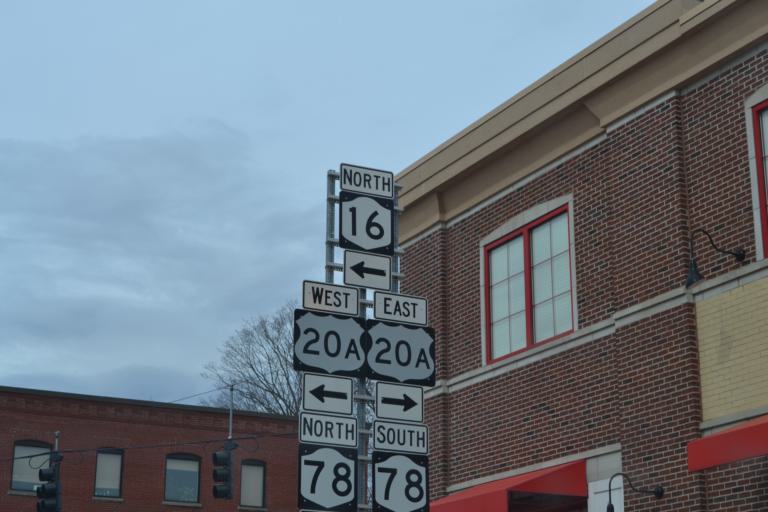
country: US
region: New York
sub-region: Erie County
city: East Aurora
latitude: 42.7676
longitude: -78.6079
